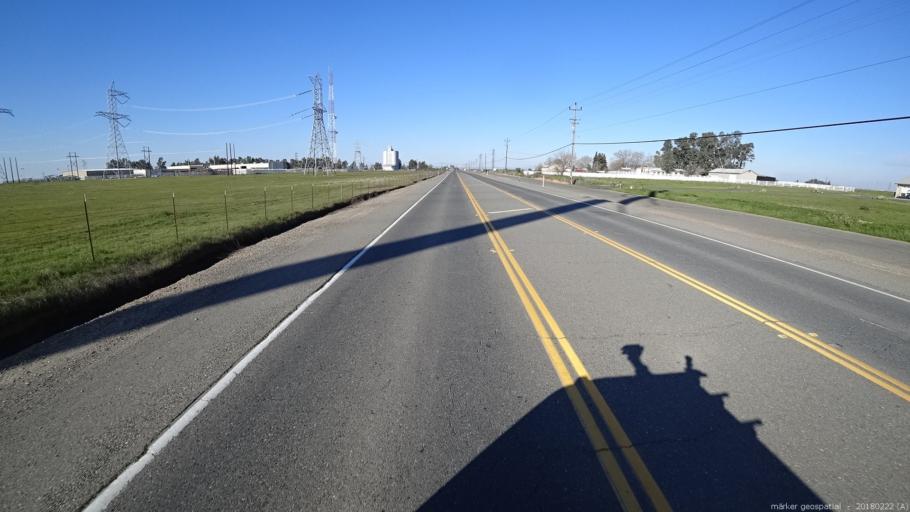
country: US
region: California
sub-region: Sacramento County
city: Elverta
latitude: 38.7144
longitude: -121.4807
